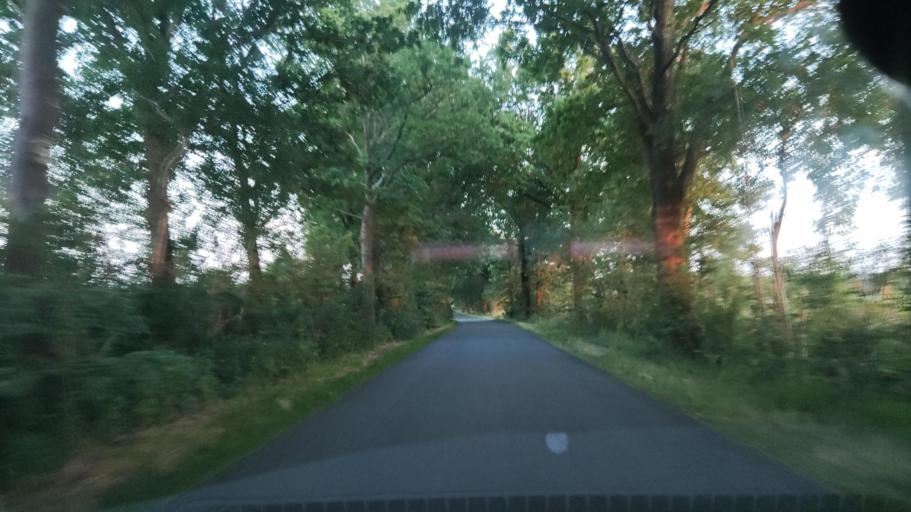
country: DE
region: Lower Saxony
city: Egestorf
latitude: 53.1349
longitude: 10.0406
